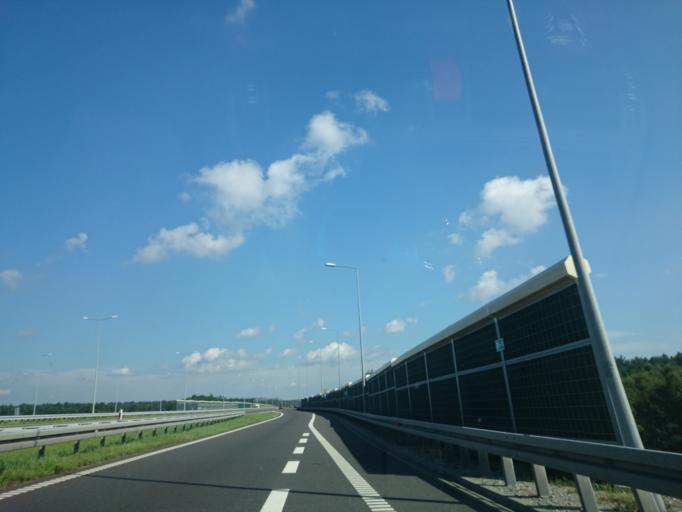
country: PL
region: Silesian Voivodeship
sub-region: Zory
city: Zory
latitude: 50.0788
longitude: 18.6638
